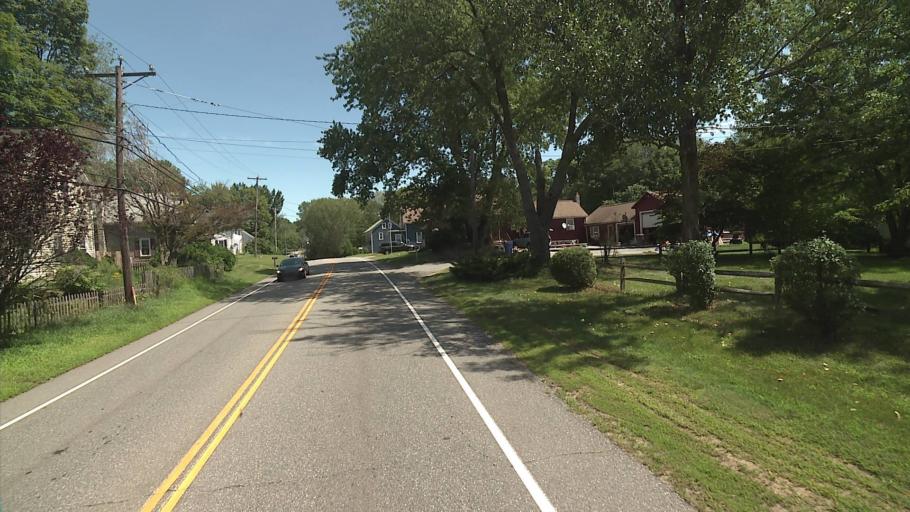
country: US
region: Connecticut
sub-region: Windham County
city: Killingly Center
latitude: 41.8471
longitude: -71.8248
